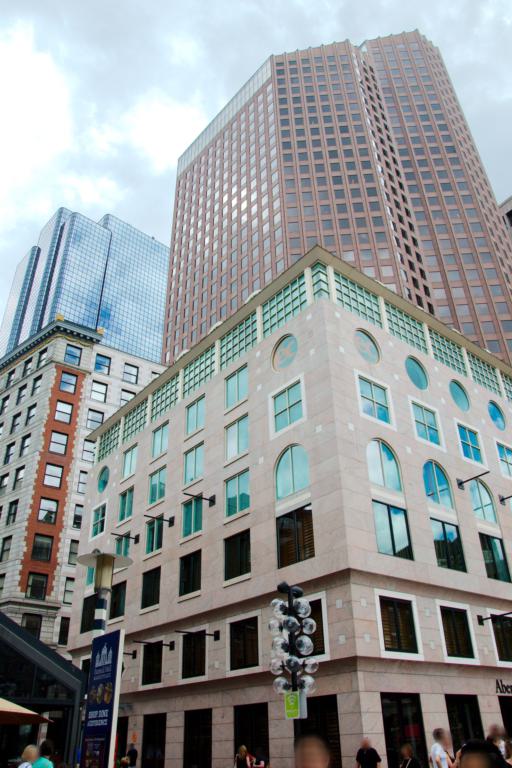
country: US
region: Massachusetts
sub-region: Suffolk County
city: Boston
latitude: 42.3600
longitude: -71.0558
